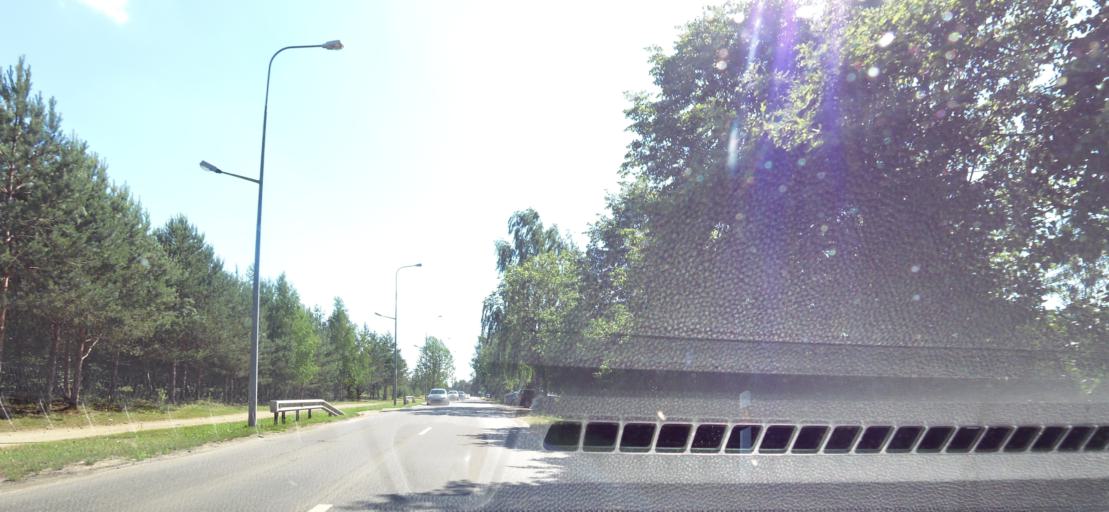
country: LT
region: Vilnius County
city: Rasos
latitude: 54.7830
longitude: 25.3446
